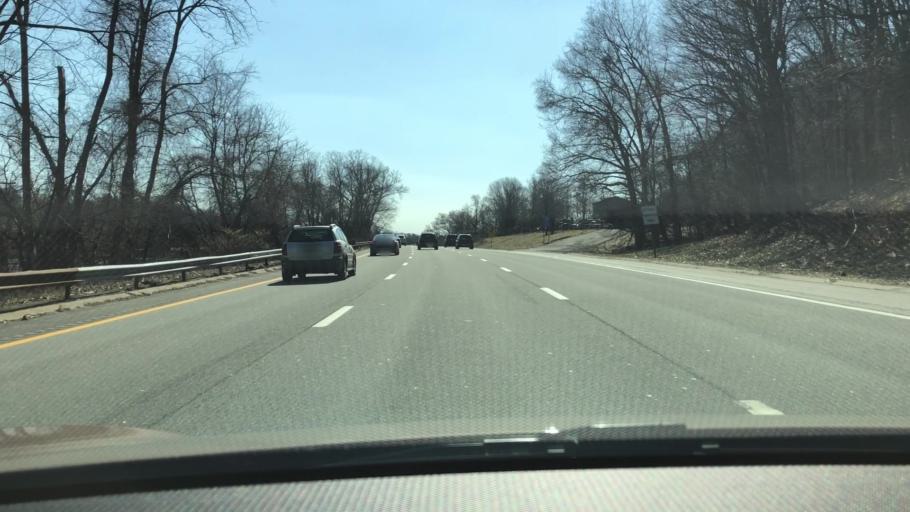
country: US
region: New York
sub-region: Westchester County
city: Tuckahoe
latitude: 40.9631
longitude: -73.8532
